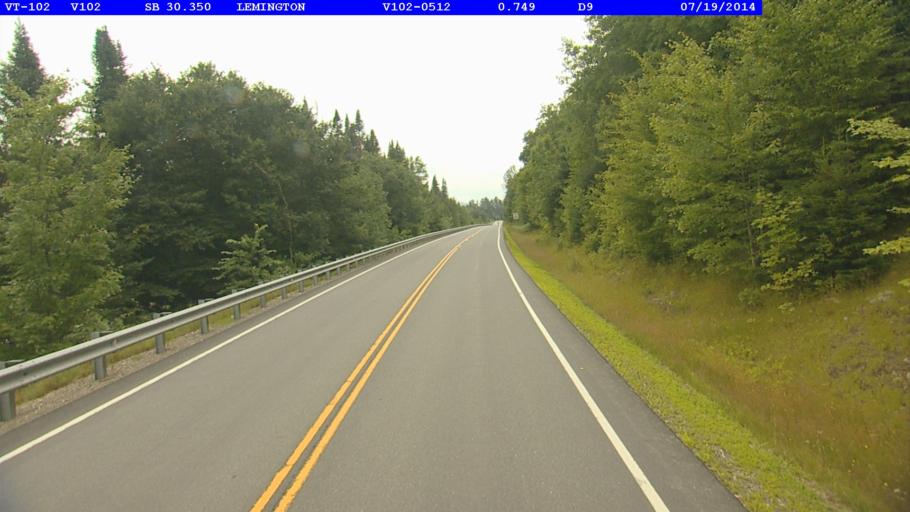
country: US
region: New Hampshire
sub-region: Coos County
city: Colebrook
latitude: 44.8352
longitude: -71.5574
